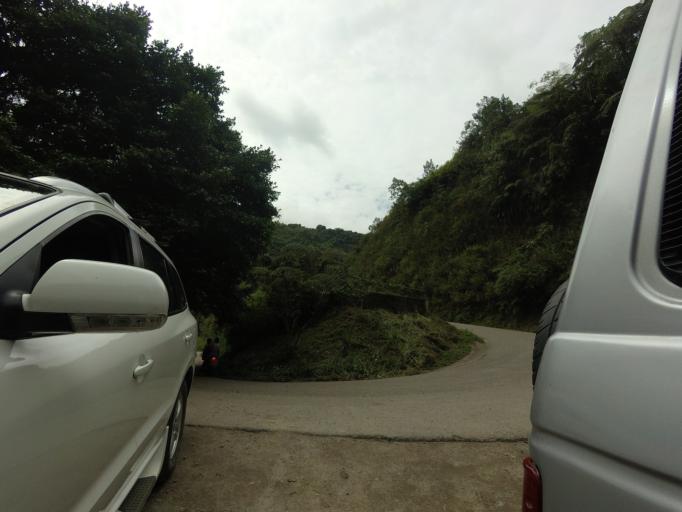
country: CO
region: Huila
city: San Agustin
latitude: 1.9270
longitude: -76.2992
